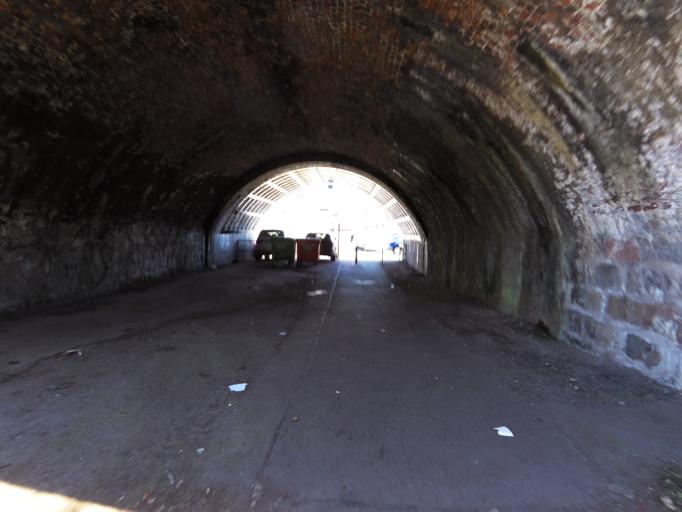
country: GB
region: Scotland
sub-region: Aberdeen City
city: Aberdeen
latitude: 57.1357
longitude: -2.0977
